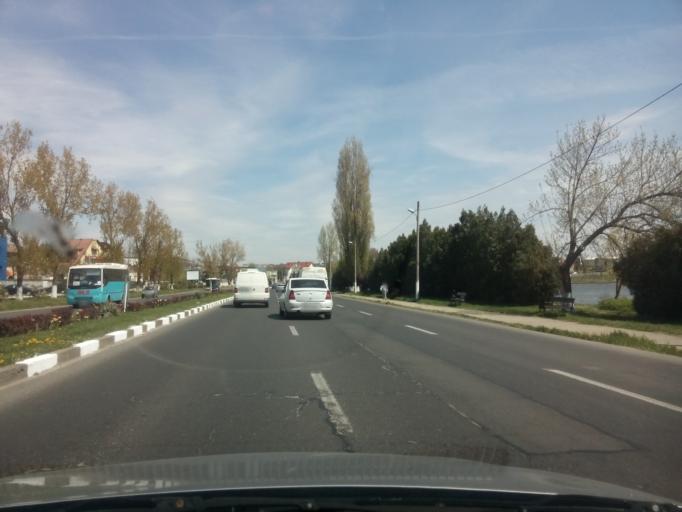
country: RO
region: Ilfov
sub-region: Comuna Pantelimon
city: Pantelimon
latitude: 44.4464
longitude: 26.2025
